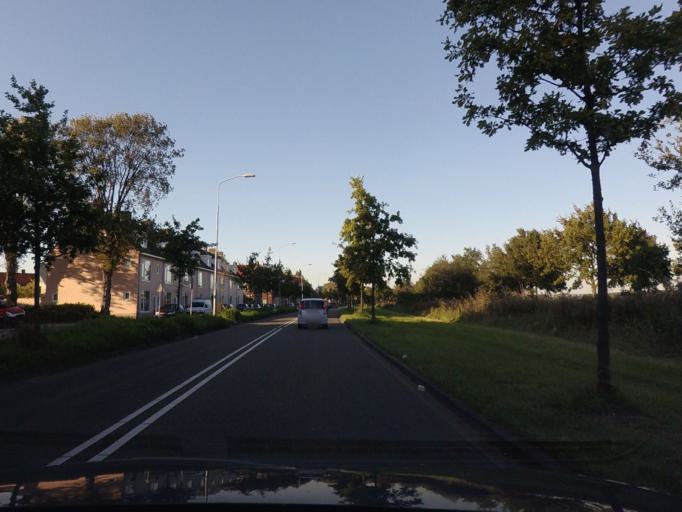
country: NL
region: North Holland
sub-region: Gemeente Bloemendaal
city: Bloemendaal
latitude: 52.4117
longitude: 4.6566
